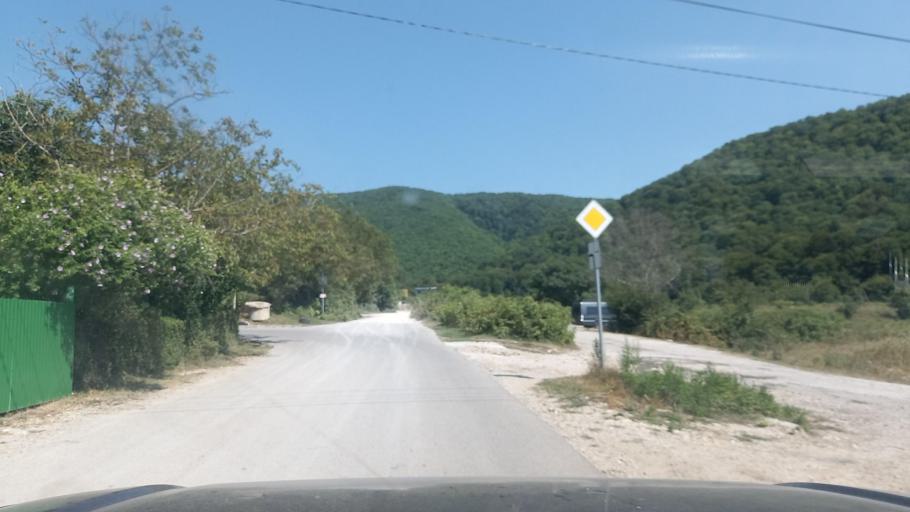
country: RU
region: Krasnodarskiy
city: Lermontovo
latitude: 44.3269
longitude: 38.7919
